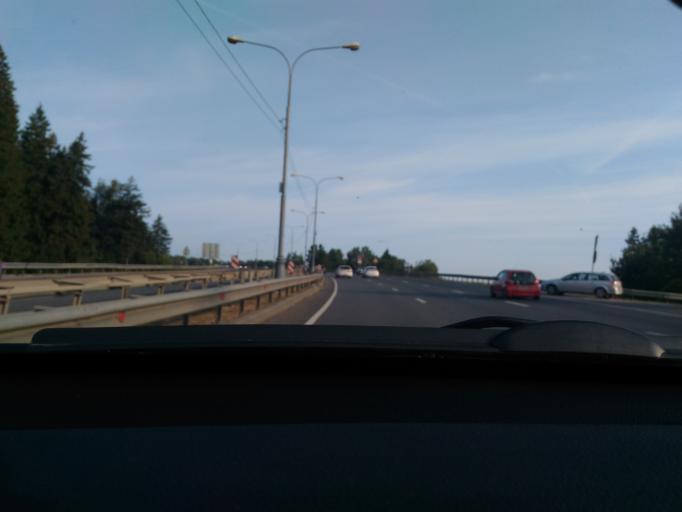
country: RU
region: Moskovskaya
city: Nekrasovskiy
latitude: 56.1222
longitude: 37.5220
